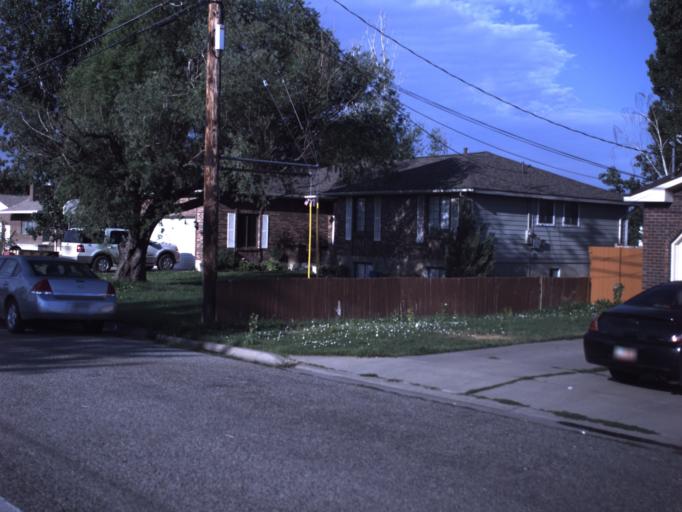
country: US
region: Utah
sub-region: Weber County
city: Plain City
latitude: 41.2922
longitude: -112.0932
